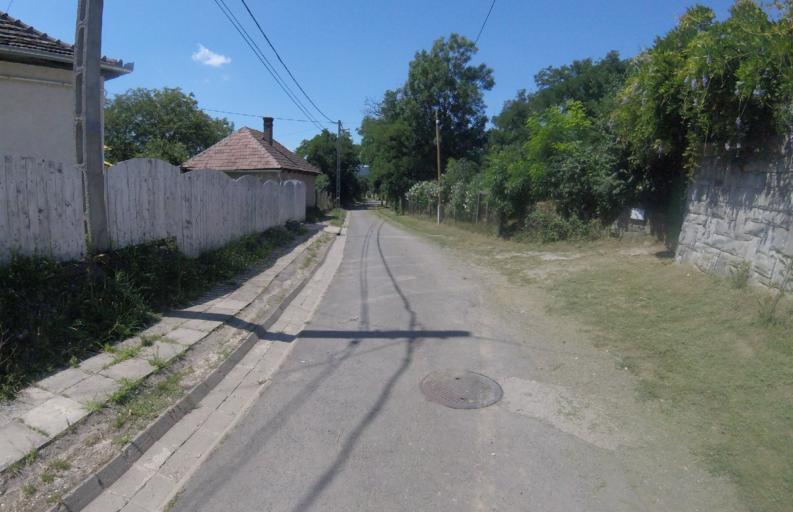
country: HU
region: Pest
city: Szob
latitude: 47.8671
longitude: 18.8759
